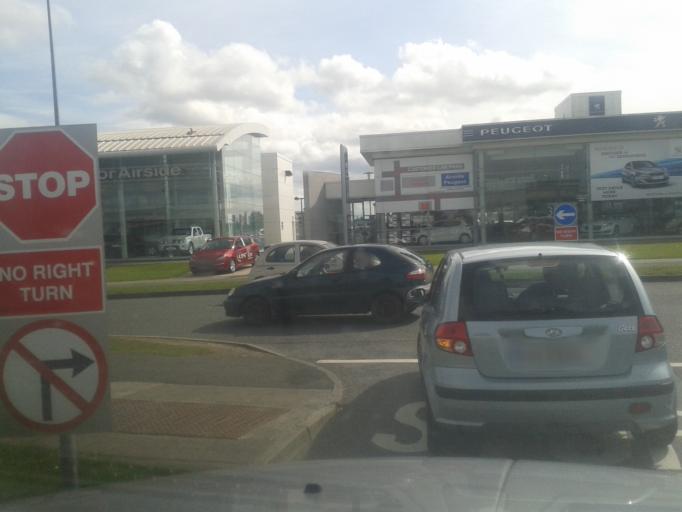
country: IE
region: Leinster
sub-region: Fingal County
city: Swords
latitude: 53.4462
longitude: -6.2233
